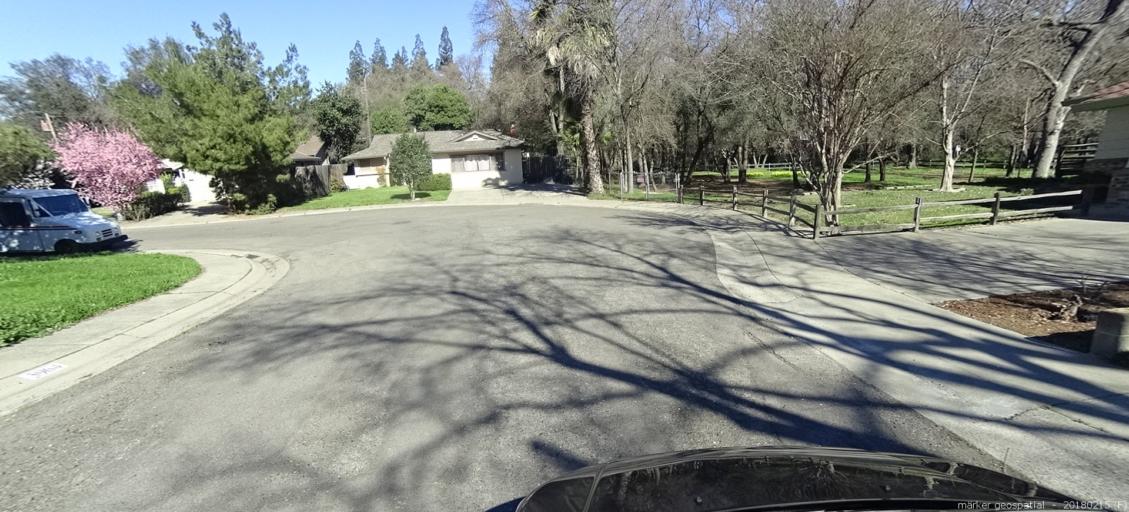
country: US
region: California
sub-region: Sacramento County
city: Foothill Farms
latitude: 38.6733
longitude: -121.3203
